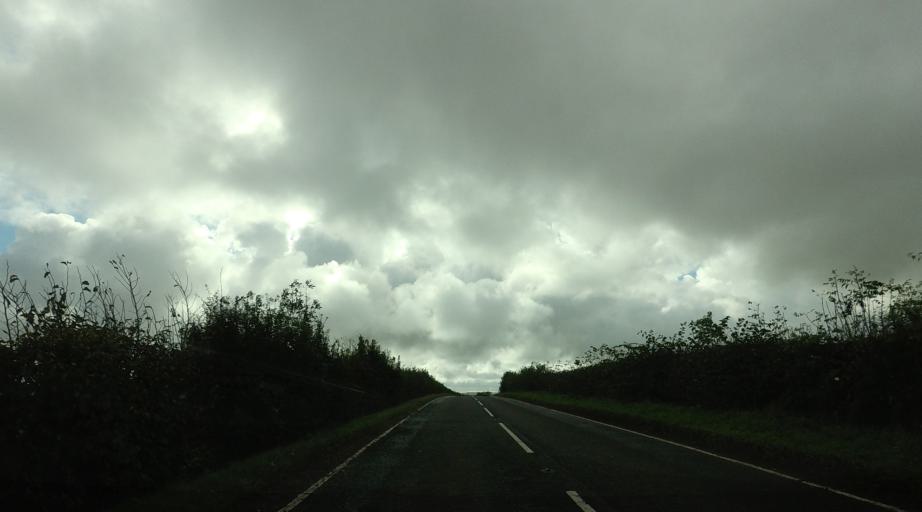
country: GB
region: Scotland
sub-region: Fife
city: Balmullo
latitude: 56.3690
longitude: -2.9323
